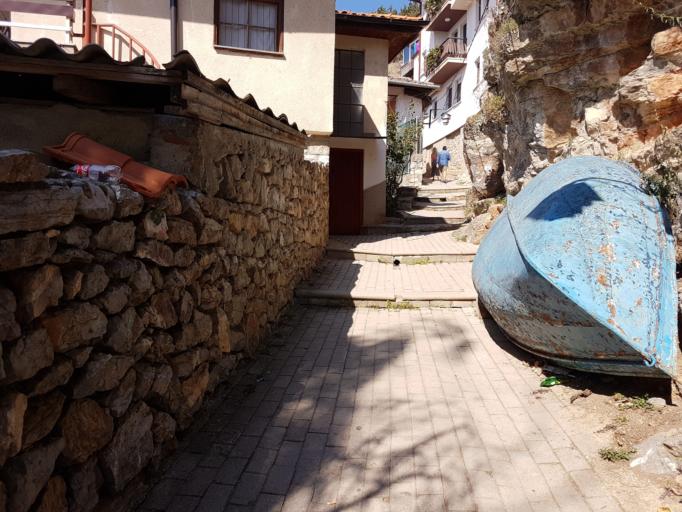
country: MK
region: Ohrid
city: Ohrid
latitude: 41.1110
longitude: 20.7911
